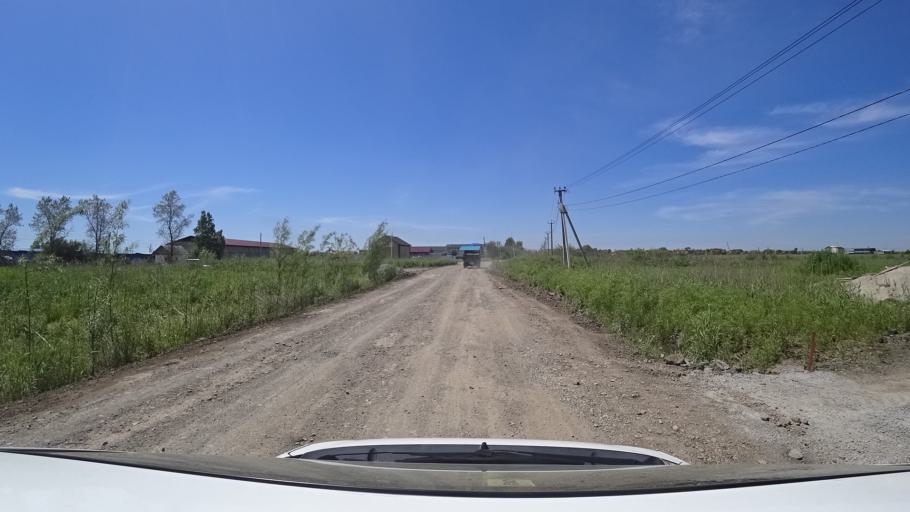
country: RU
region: Khabarovsk Krai
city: Topolevo
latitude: 48.5125
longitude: 135.1904
